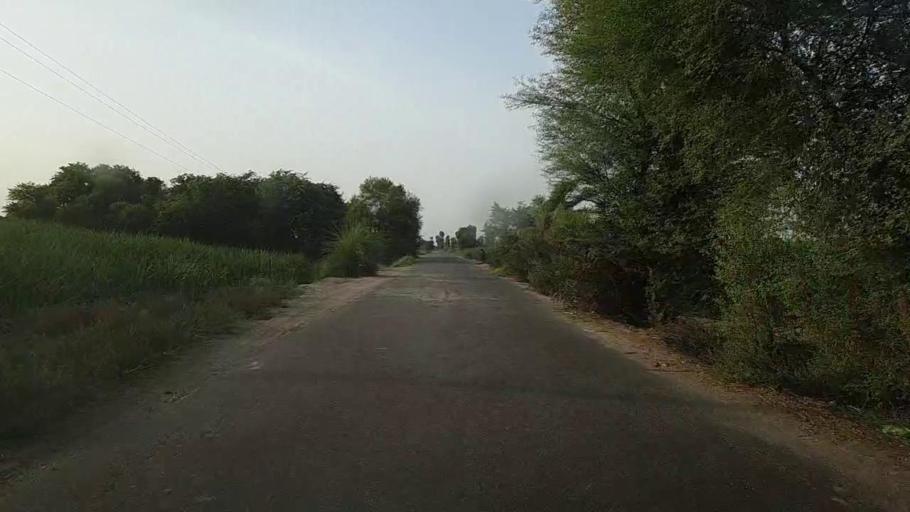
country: PK
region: Sindh
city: Ubauro
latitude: 28.1829
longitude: 69.8283
